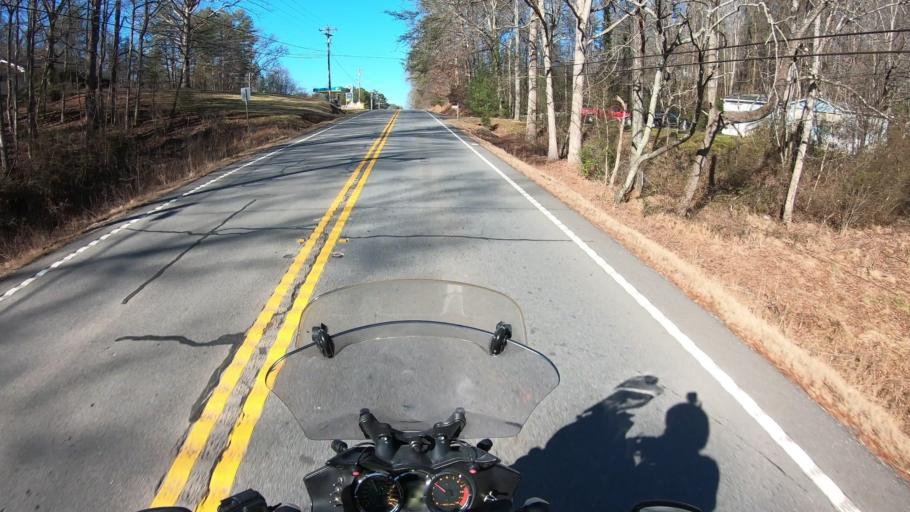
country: US
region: Georgia
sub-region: Fannin County
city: McCaysville
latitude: 34.9685
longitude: -84.3284
